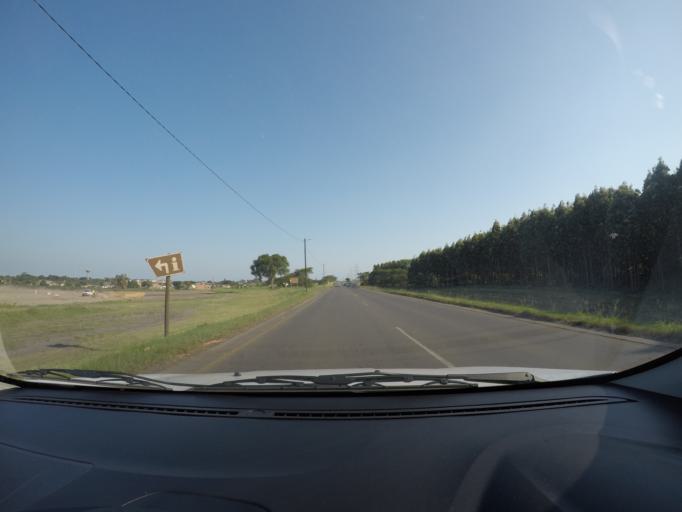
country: ZA
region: KwaZulu-Natal
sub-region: uThungulu District Municipality
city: Richards Bay
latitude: -28.7193
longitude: 32.0326
